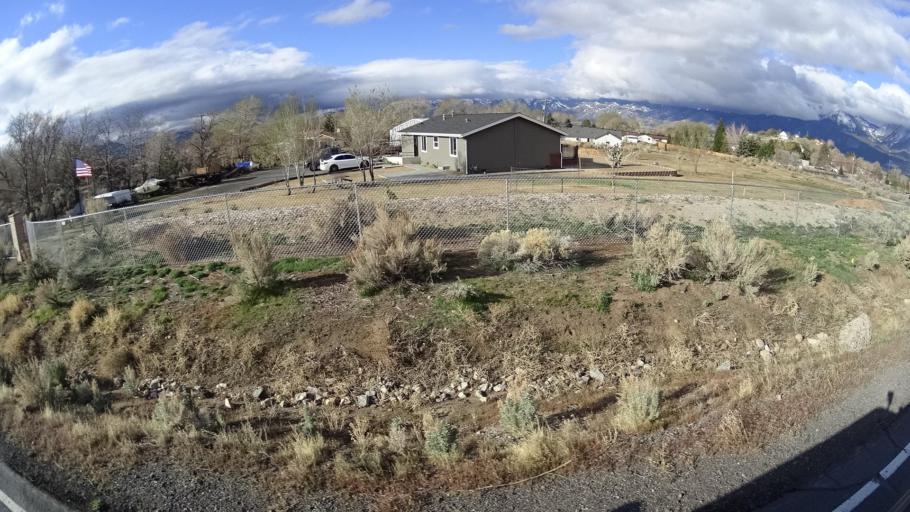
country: US
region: Nevada
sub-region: Storey County
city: Virginia City
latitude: 39.2870
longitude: -119.7607
